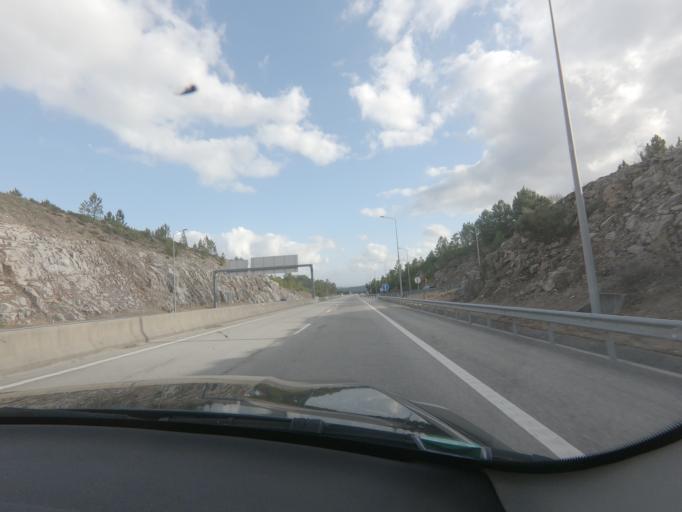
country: PT
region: Viseu
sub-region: Viseu
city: Abraveses
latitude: 40.6759
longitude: -7.9683
